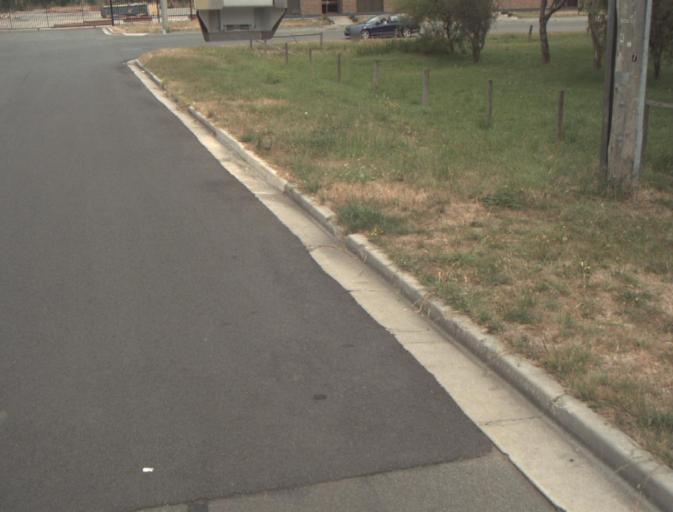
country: AU
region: Tasmania
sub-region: Launceston
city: Newnham
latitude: -41.4092
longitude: 147.1358
